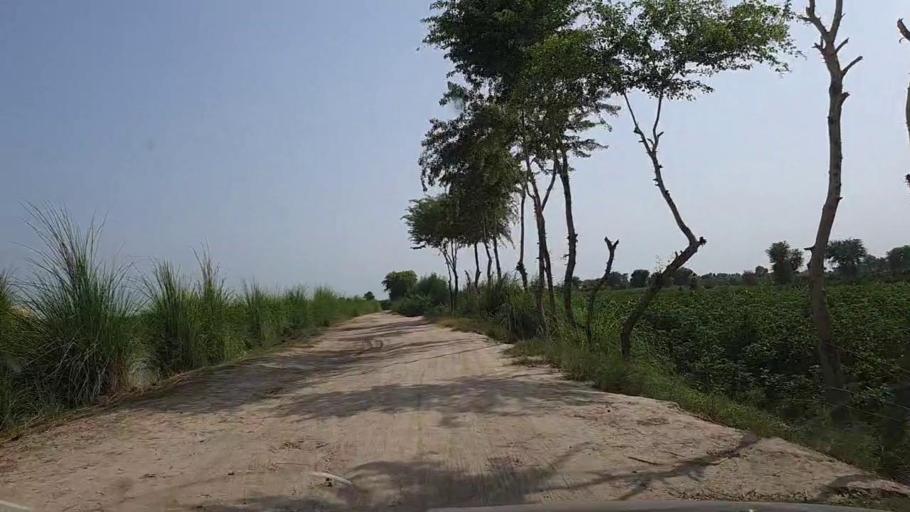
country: PK
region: Sindh
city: Ghotki
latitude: 28.0593
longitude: 69.3806
